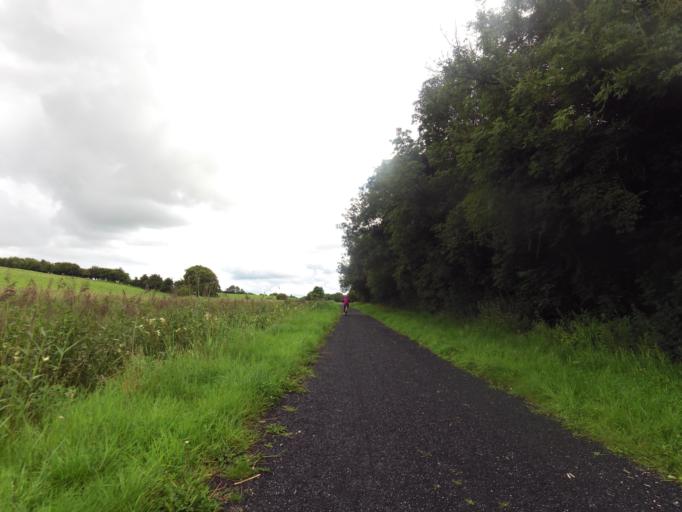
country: IE
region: Leinster
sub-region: An Iarmhi
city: An Muileann gCearr
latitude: 53.5180
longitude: -7.4348
